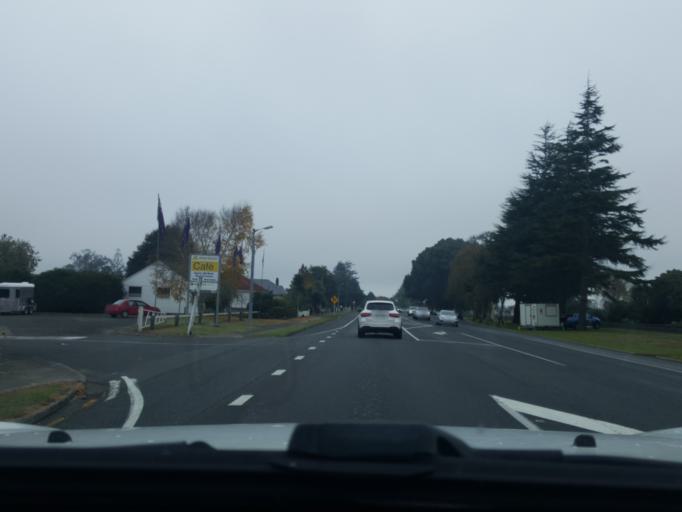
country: NZ
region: Waikato
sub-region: Waikato District
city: Ngaruawahia
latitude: -37.5418
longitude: 175.1583
